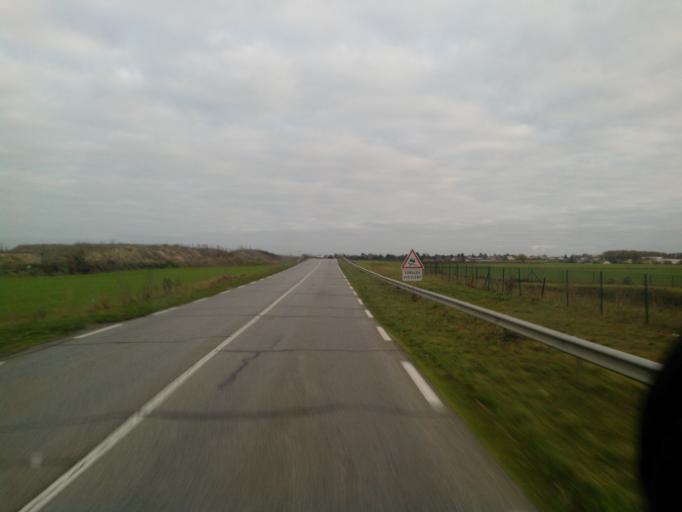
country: FR
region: Poitou-Charentes
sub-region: Departement de la Vienne
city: Vouille
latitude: 46.6492
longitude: 0.1509
